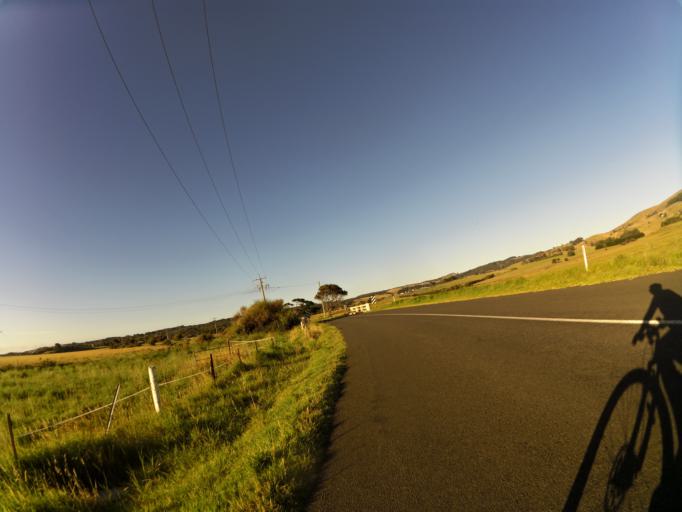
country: AU
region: Victoria
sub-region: Colac-Otway
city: Apollo Bay
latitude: -38.7615
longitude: 143.6622
